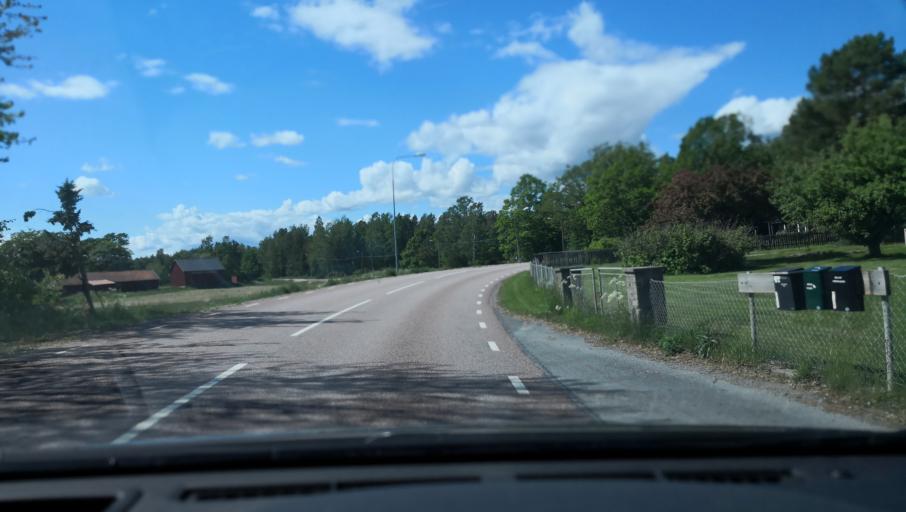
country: SE
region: Vaestmanland
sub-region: Kungsors Kommun
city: Kungsoer
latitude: 59.2895
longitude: 16.0619
